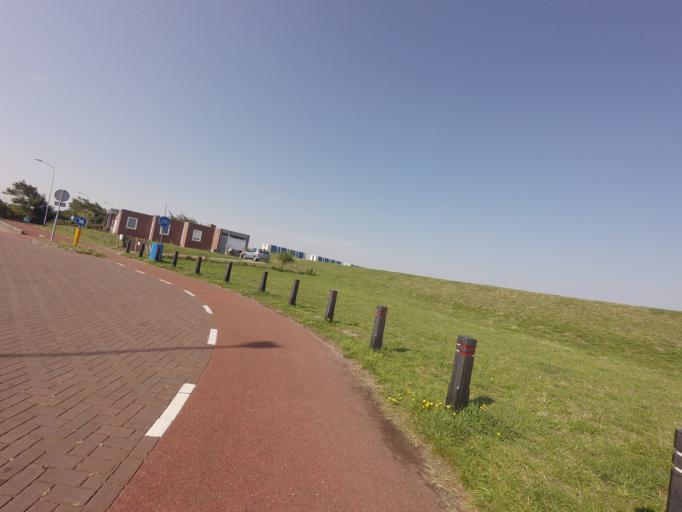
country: NL
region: Friesland
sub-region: Gemeente Dongeradeel
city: Anjum
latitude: 53.4110
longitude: 6.1965
